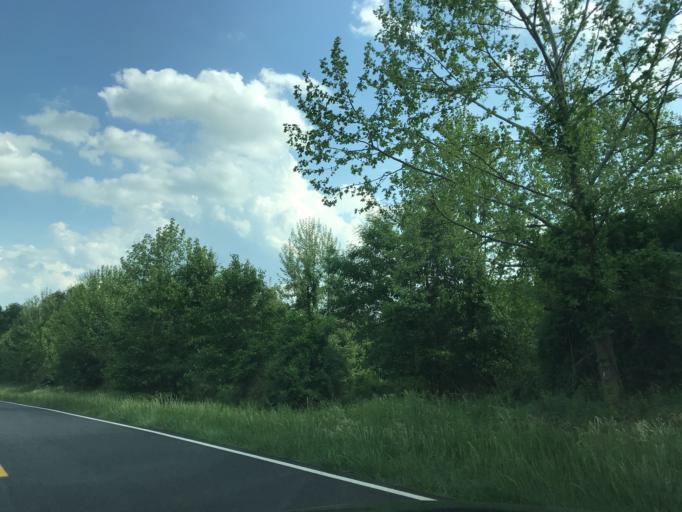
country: US
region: Maryland
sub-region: Harford County
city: Bel Air North
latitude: 39.5520
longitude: -76.3951
